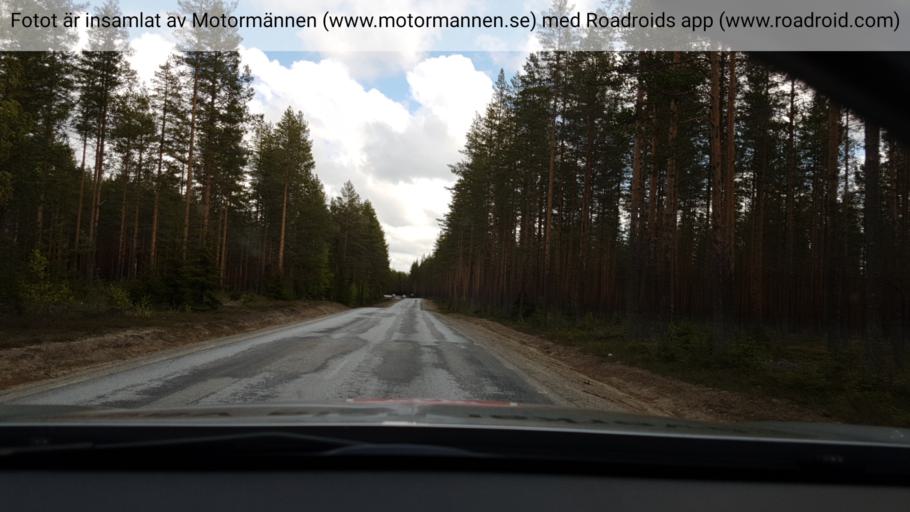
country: SE
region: Vaesterbotten
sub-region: Vindelns Kommun
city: Vindeln
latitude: 64.1682
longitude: 19.7764
